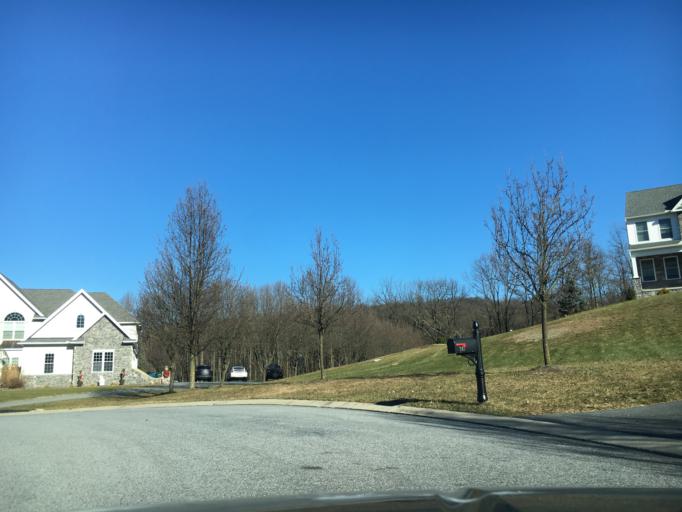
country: US
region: Pennsylvania
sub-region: Berks County
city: Fleetwood
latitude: 40.4297
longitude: -75.8093
